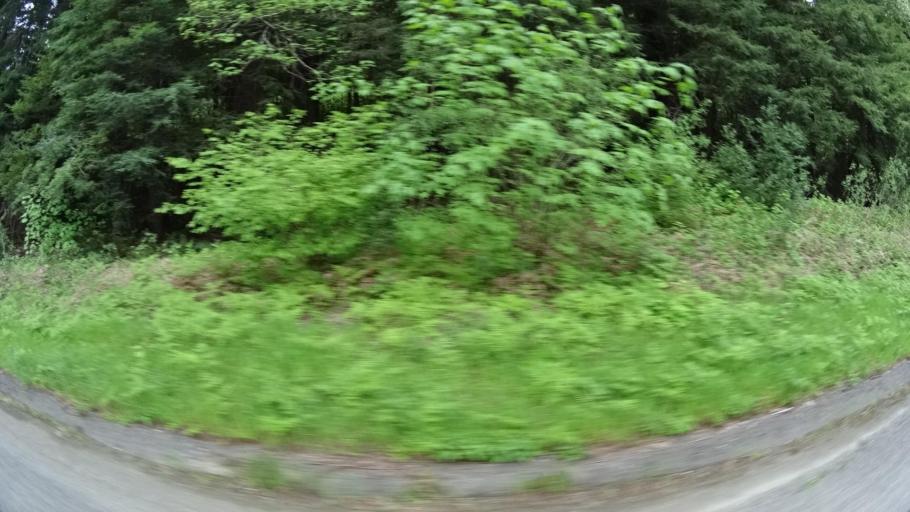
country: US
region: California
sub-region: Humboldt County
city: Redway
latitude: 40.2274
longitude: -123.8288
